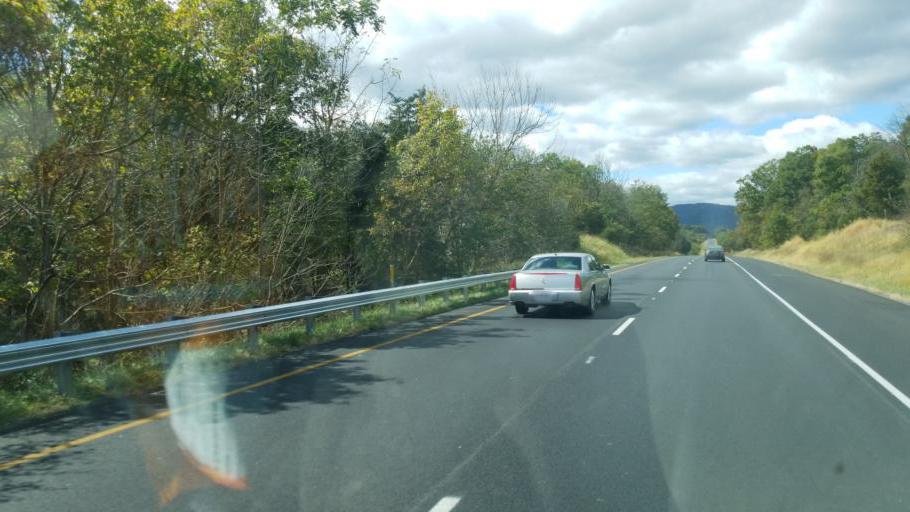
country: US
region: Maryland
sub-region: Washington County
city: Wilson-Conococheague
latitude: 39.6521
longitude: -77.8899
